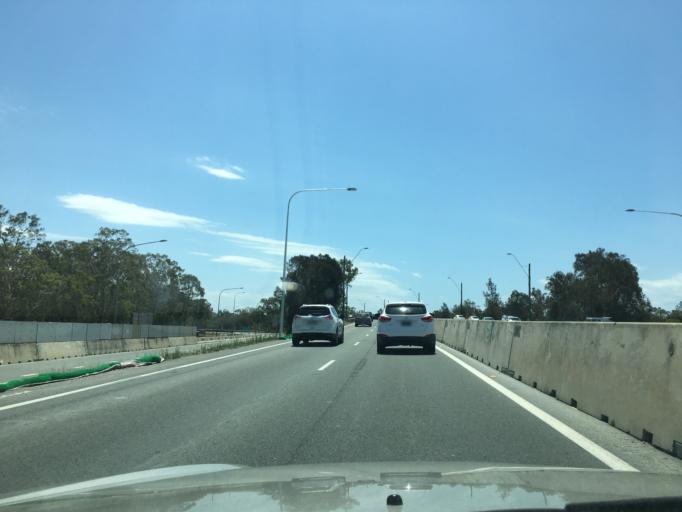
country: AU
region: Queensland
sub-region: Brisbane
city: Deagon
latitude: -27.3441
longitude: 153.0767
